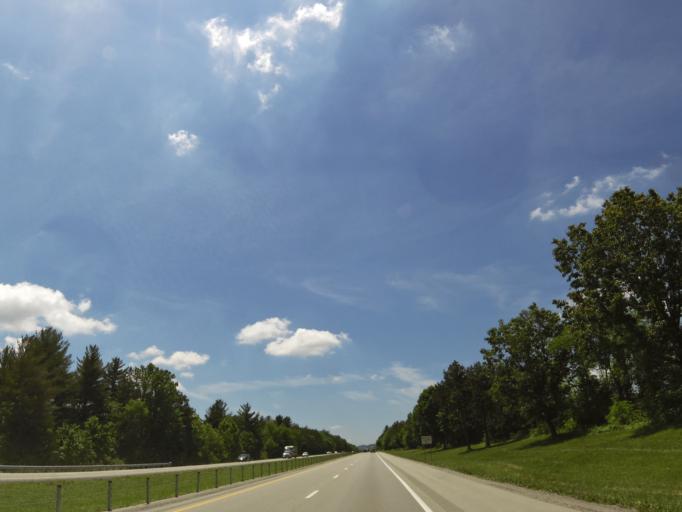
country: US
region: Kentucky
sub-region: Whitley County
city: Williamsburg
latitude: 36.7757
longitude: -84.1703
